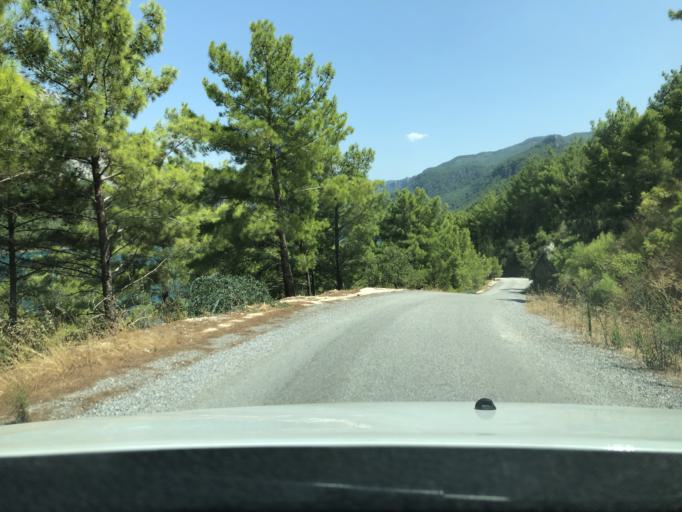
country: TR
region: Antalya
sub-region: Manavgat
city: Manavgat
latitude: 36.9115
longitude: 31.5477
